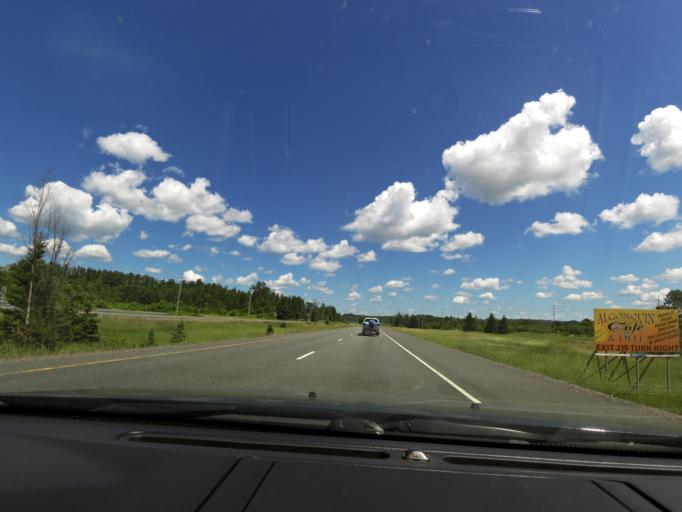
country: CA
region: Ontario
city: Huntsville
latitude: 45.2519
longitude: -79.2970
